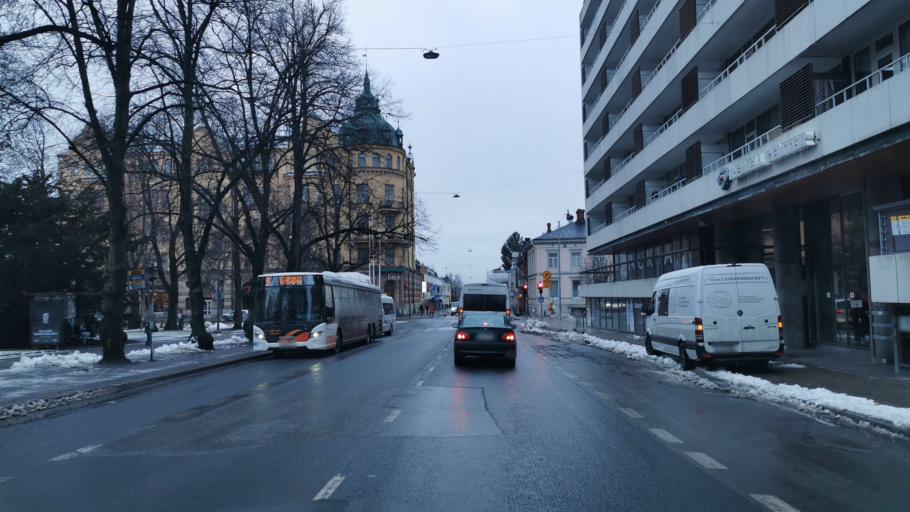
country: FI
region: Ostrobothnia
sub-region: Vaasa
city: Vaasa
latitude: 63.0952
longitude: 21.6131
